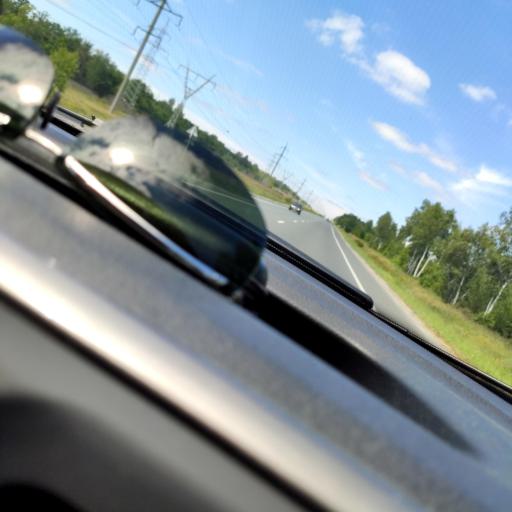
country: RU
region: Samara
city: Bogatyr'
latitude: 53.4936
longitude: 49.9677
